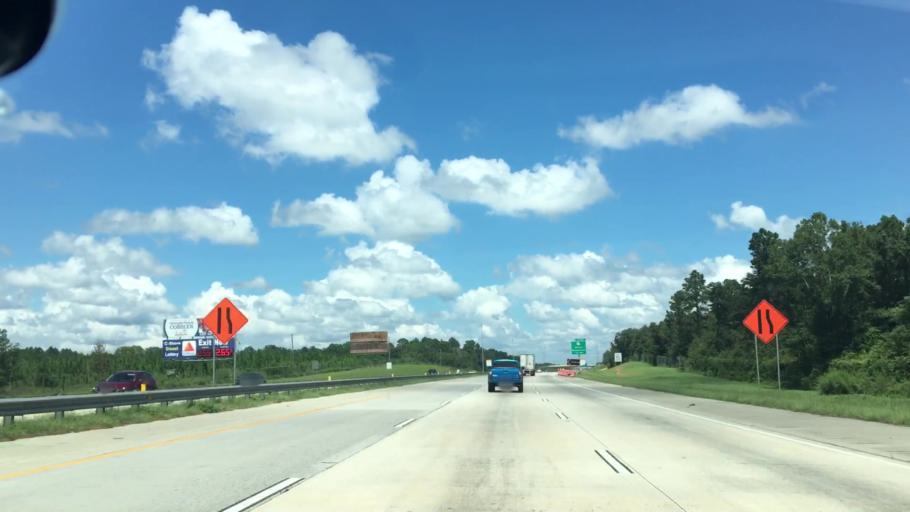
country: US
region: Georgia
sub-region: Dooly County
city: Vienna
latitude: 32.1111
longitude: -83.7627
